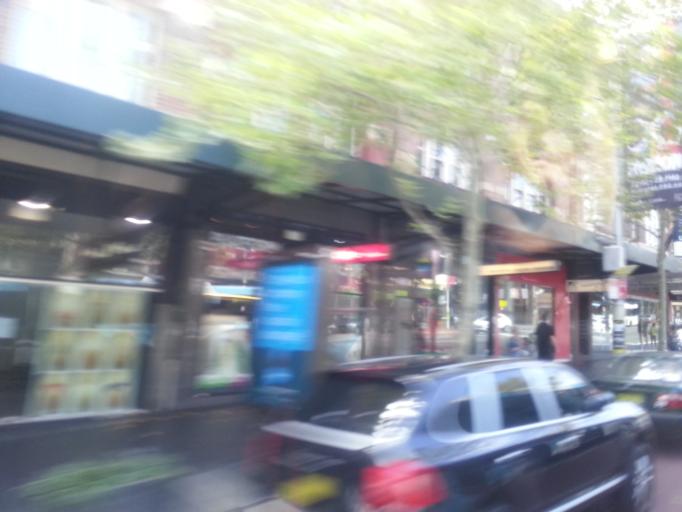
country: AU
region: New South Wales
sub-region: City of Sydney
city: Darlinghurst
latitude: -33.8787
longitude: 151.2147
